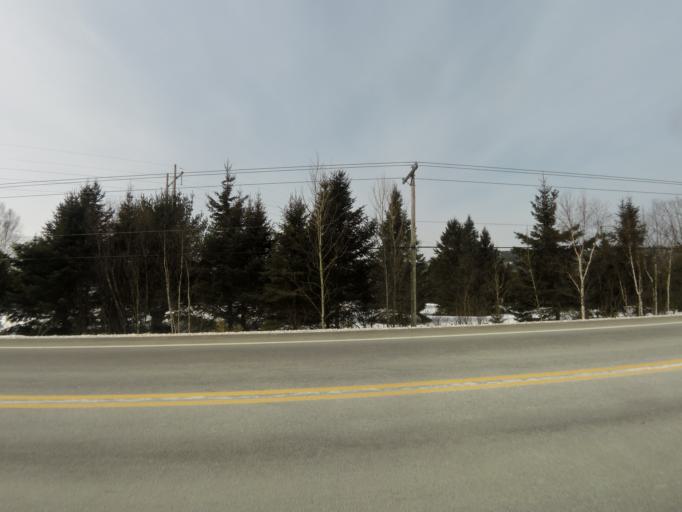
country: CA
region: Quebec
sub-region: Outaouais
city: Maniwaki
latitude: 46.1951
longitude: -75.6753
